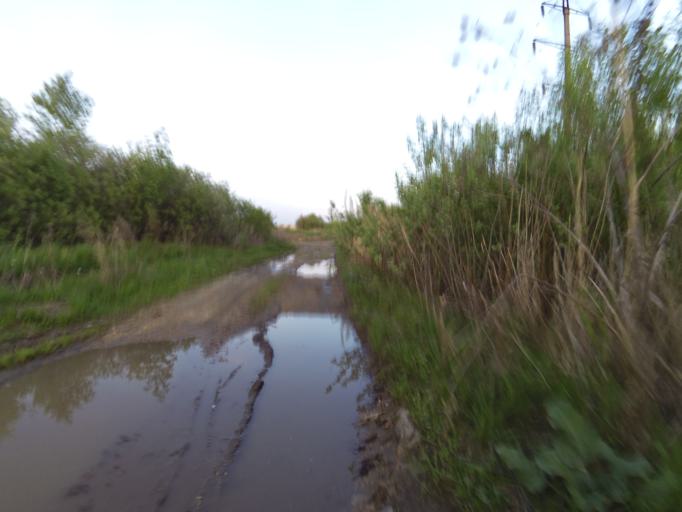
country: RU
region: Sverdlovsk
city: Shirokaya Rechka
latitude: 56.8373
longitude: 60.5169
